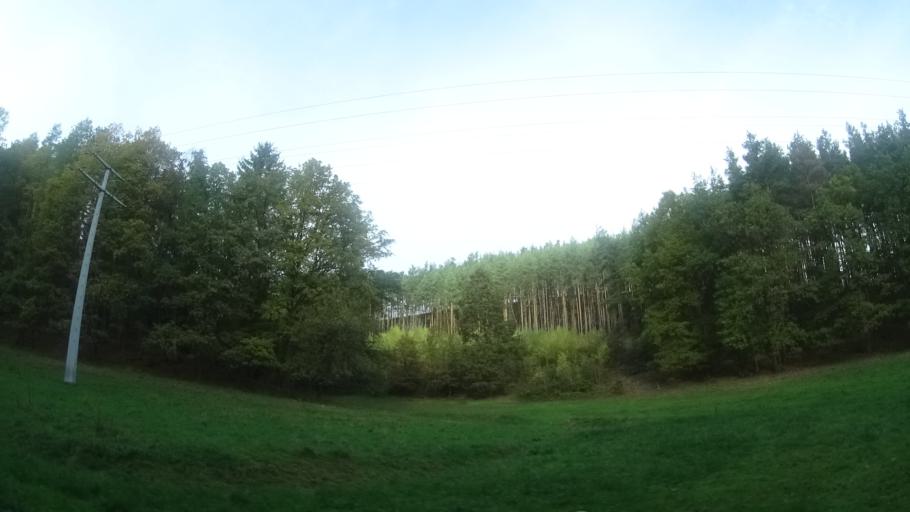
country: DE
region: Thuringia
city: Rudolstadt
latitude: 50.6980
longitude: 11.3891
